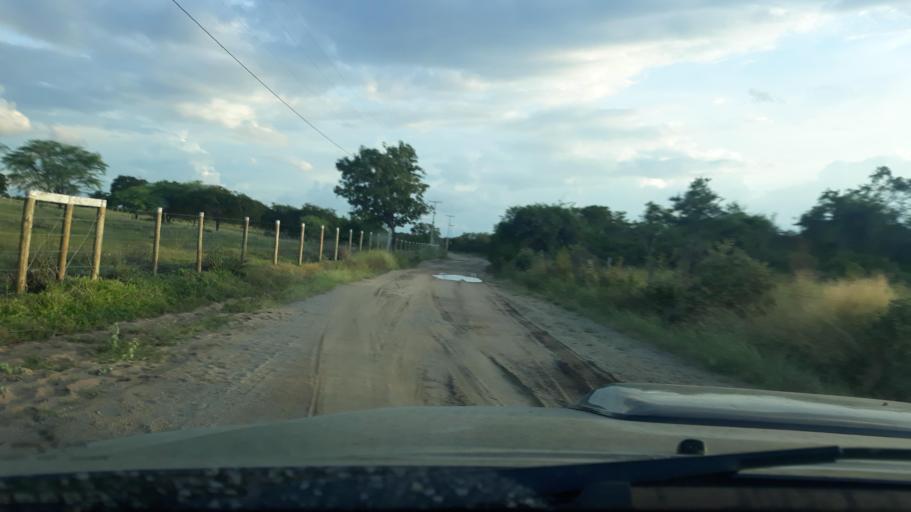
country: BR
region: Bahia
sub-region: Riacho De Santana
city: Riacho de Santana
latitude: -13.8796
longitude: -43.0209
